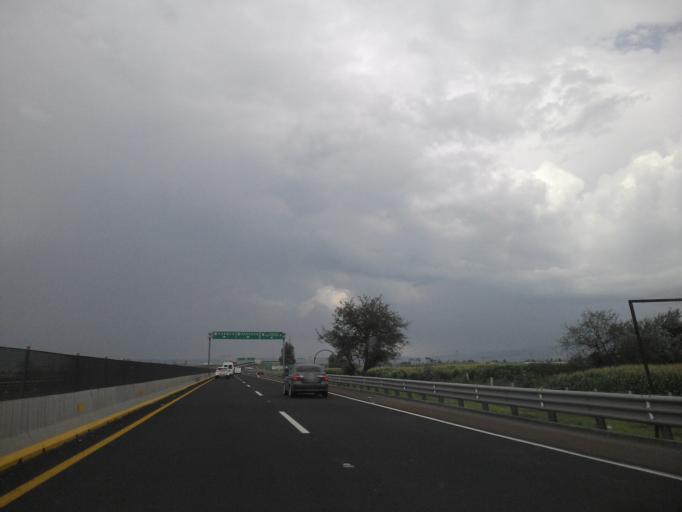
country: MX
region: Hidalgo
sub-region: Tula de Allende
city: Residencial Arboledas
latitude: 20.0978
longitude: -99.2894
